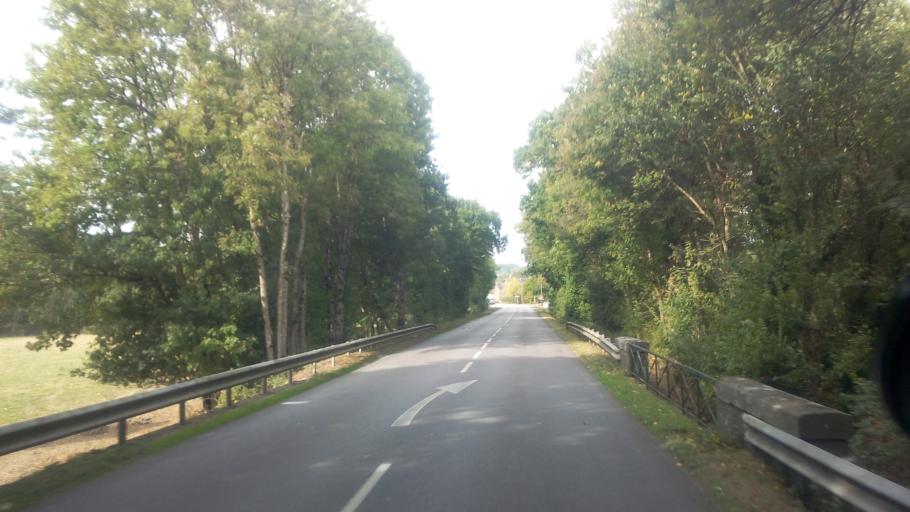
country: FR
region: Brittany
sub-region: Departement du Morbihan
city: La Gacilly
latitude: 47.7490
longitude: -2.1254
